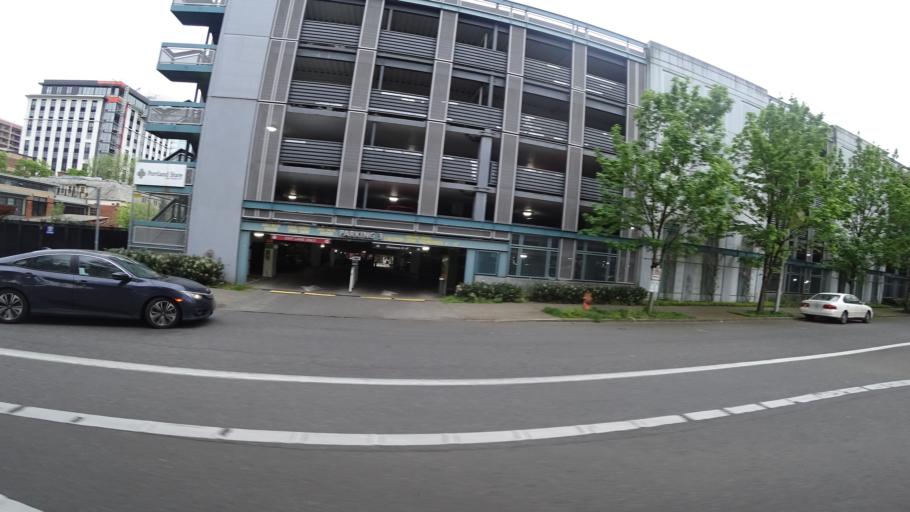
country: US
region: Oregon
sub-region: Multnomah County
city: Portland
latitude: 45.5142
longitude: -122.6888
